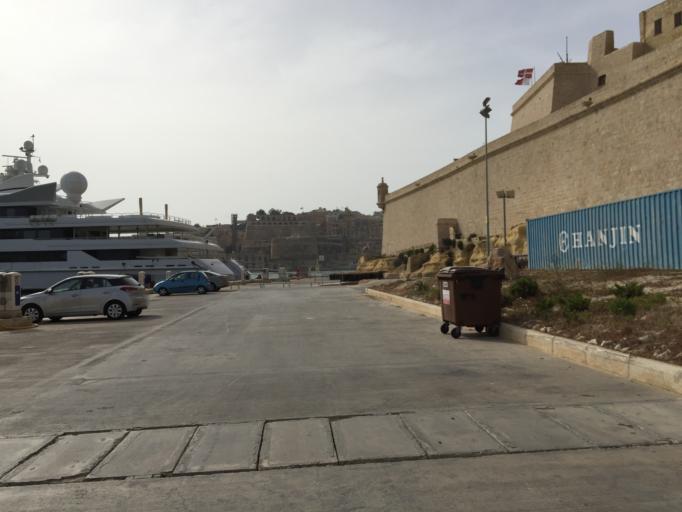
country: MT
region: Il-Birgu
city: Vittoriosa
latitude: 35.8914
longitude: 14.5180
